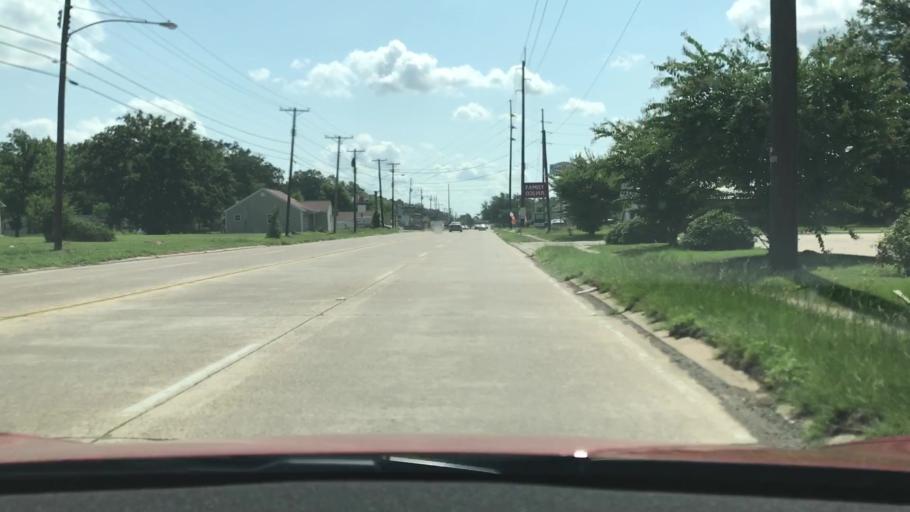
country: US
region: Louisiana
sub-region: Bossier Parish
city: Bossier City
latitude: 32.4420
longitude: -93.7688
